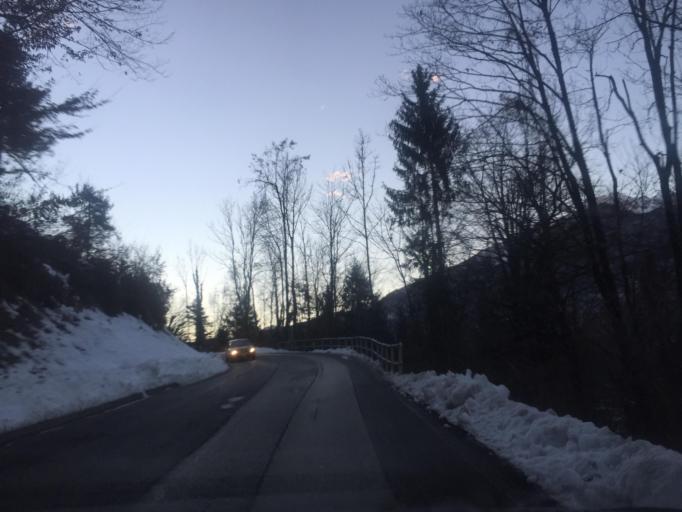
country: IT
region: Friuli Venezia Giulia
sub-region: Provincia di Udine
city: Villa Santina
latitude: 46.4214
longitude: 12.9166
